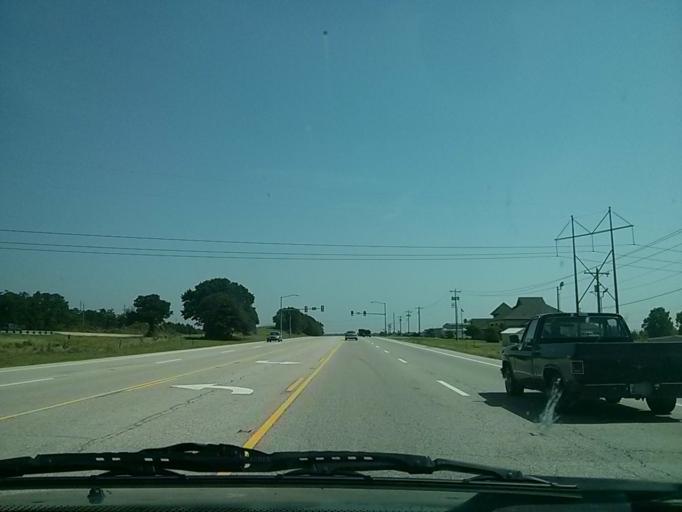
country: US
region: Oklahoma
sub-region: Tulsa County
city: Oakhurst
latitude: 36.0550
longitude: -96.0735
